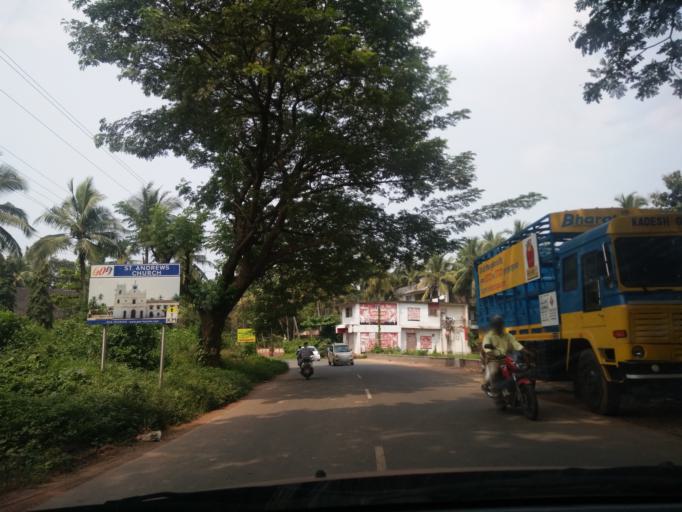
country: IN
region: Goa
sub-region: North Goa
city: Goa Velha
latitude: 15.4410
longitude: 73.8876
